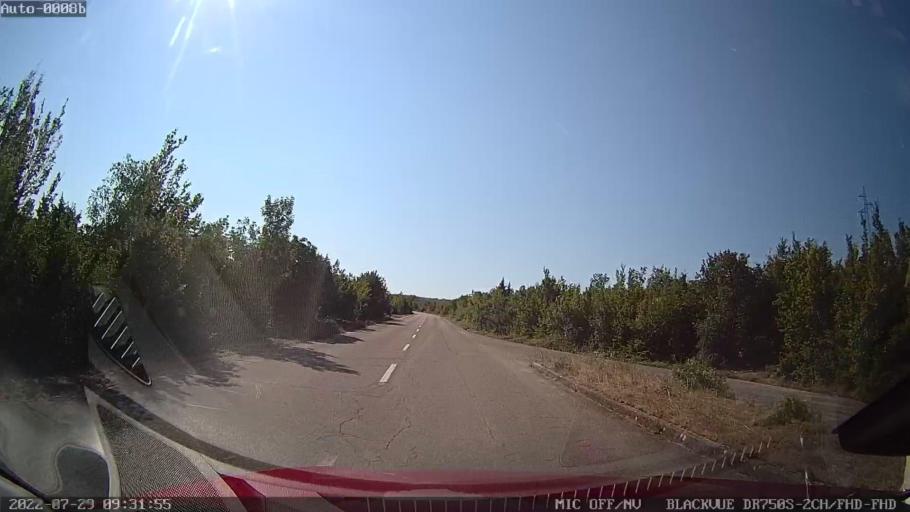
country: HR
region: Zadarska
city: Obrovac
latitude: 44.1855
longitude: 15.7048
